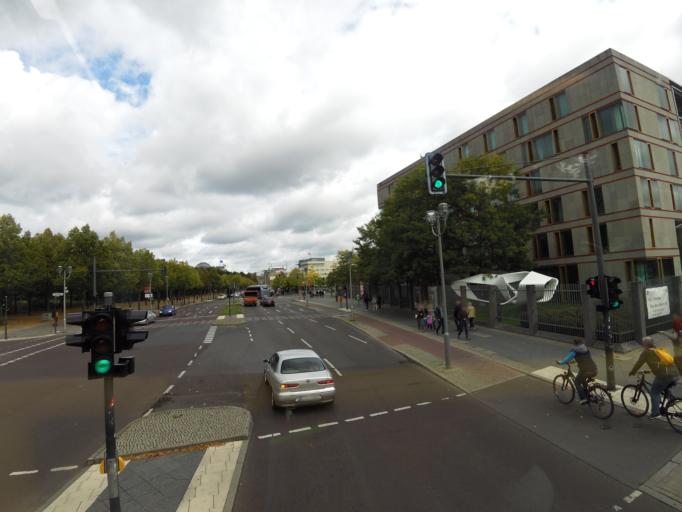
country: DE
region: Berlin
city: Tiergarten Bezirk
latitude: 52.5124
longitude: 13.3771
